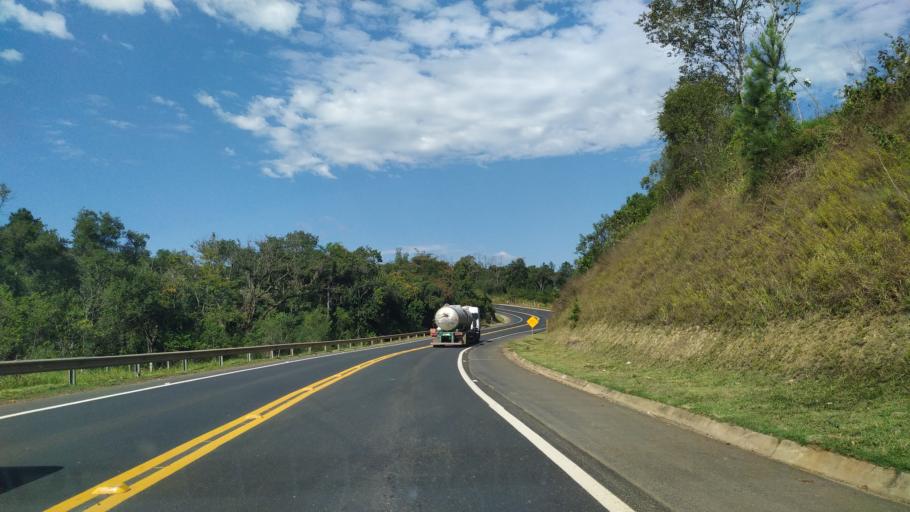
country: BR
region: Parana
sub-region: Telemaco Borba
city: Telemaco Borba
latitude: -24.2738
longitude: -50.7162
